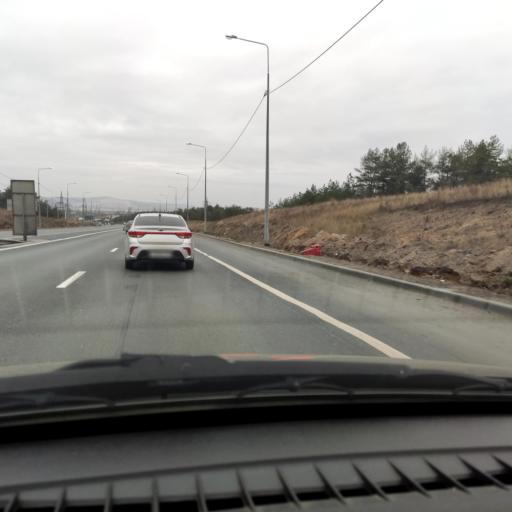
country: RU
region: Samara
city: Zhigulevsk
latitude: 53.4942
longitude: 49.5289
